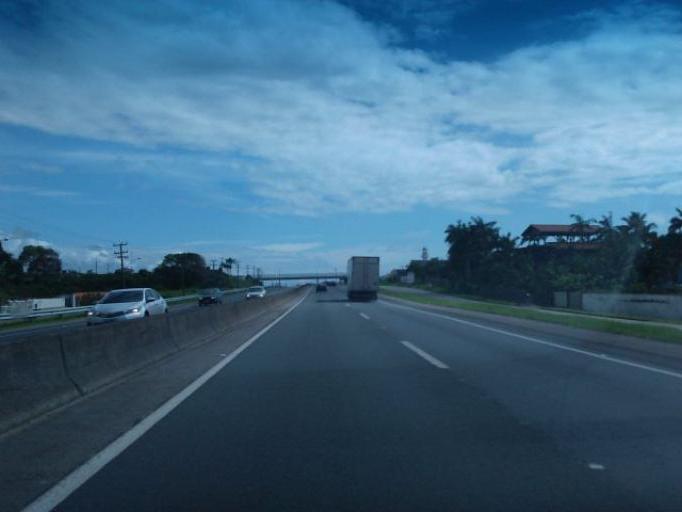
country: BR
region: Santa Catarina
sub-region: Barra Velha
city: Barra Velha
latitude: -26.6771
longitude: -48.6917
